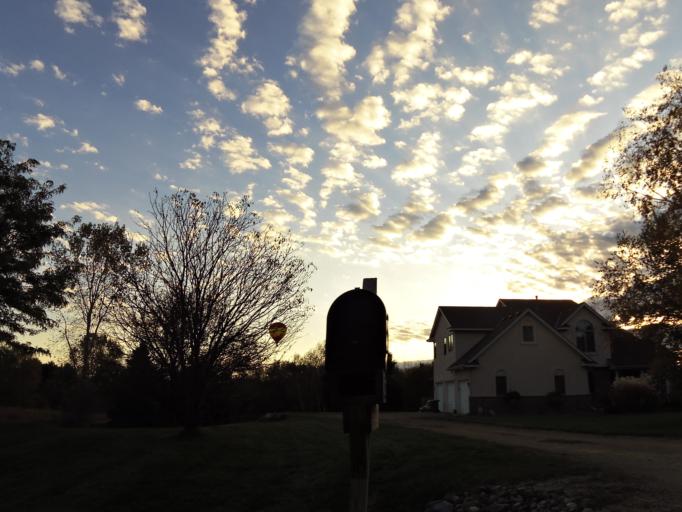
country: US
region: Minnesota
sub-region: Washington County
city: Lakeland
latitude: 44.9801
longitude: -92.8054
